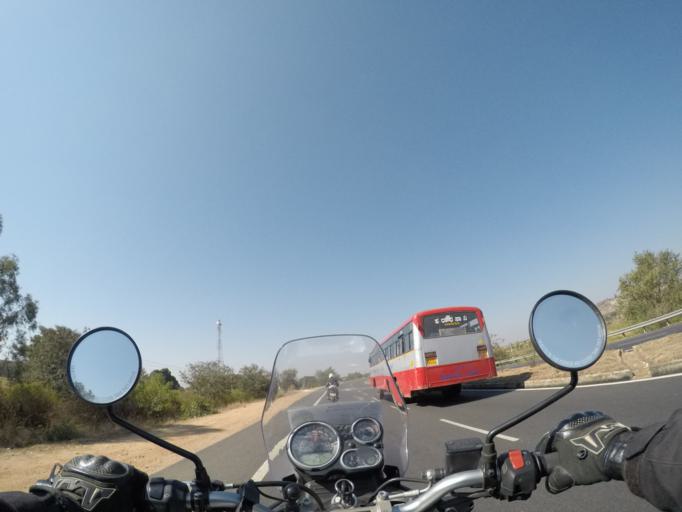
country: IN
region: Karnataka
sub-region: Mandya
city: Belluru
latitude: 12.9689
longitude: 76.7972
